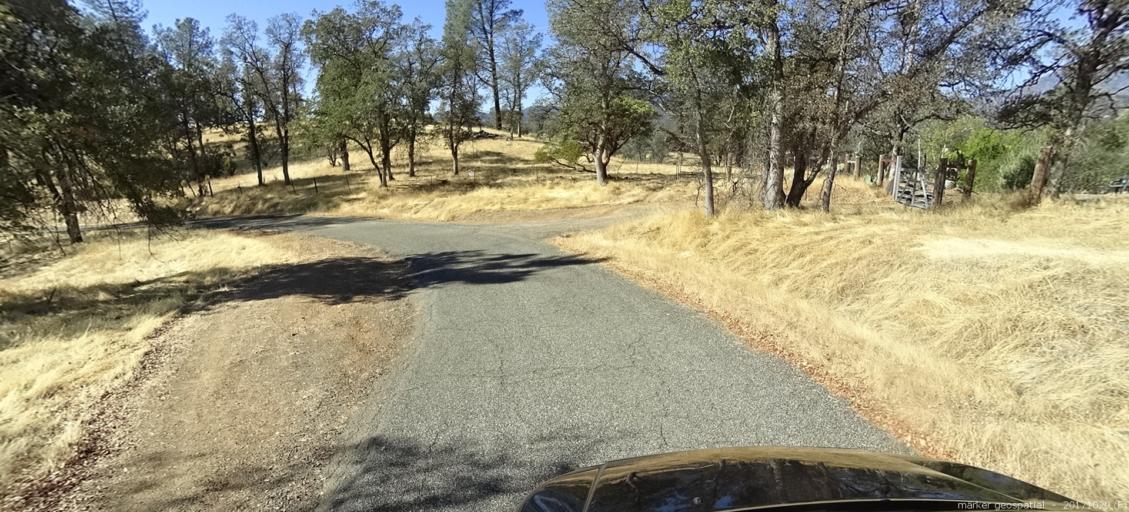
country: US
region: California
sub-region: Shasta County
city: Shasta
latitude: 40.4818
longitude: -122.6239
